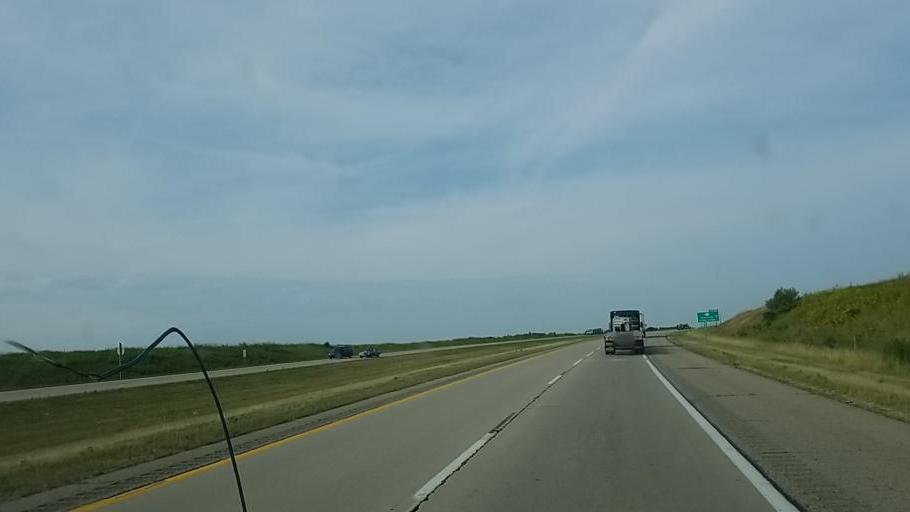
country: US
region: Michigan
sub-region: Eaton County
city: Potterville
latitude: 42.6253
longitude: -84.7303
